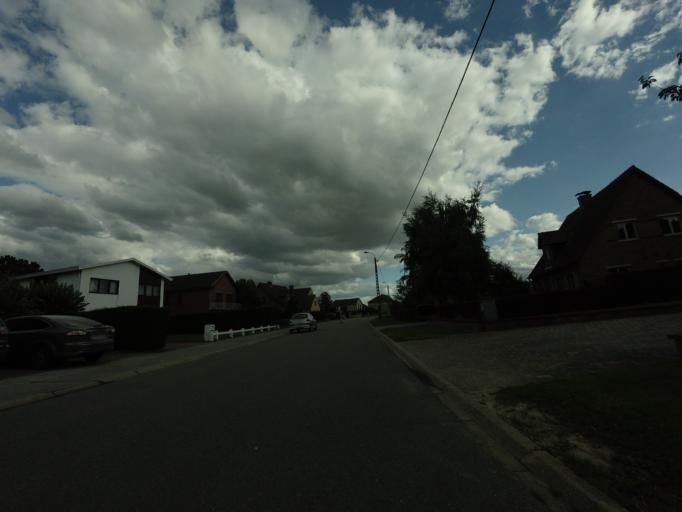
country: BE
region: Flanders
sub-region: Provincie Vlaams-Brabant
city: Kapelle-op-den-Bos
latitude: 51.0033
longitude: 4.3556
